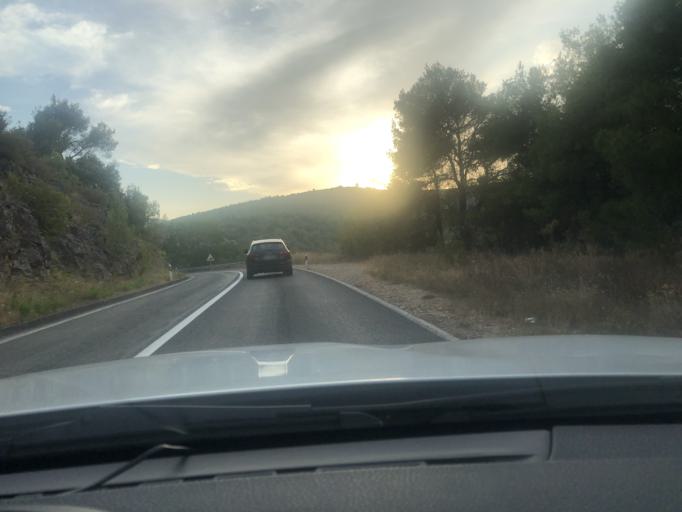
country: HR
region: Splitsko-Dalmatinska
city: Stari Grad
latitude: 43.1714
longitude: 16.5657
